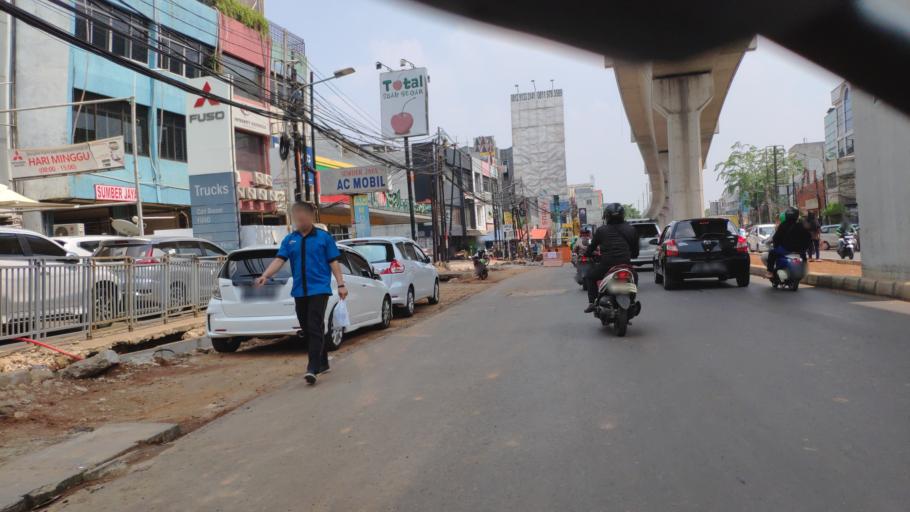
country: ID
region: Banten
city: South Tangerang
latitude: -6.2882
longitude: 106.7953
